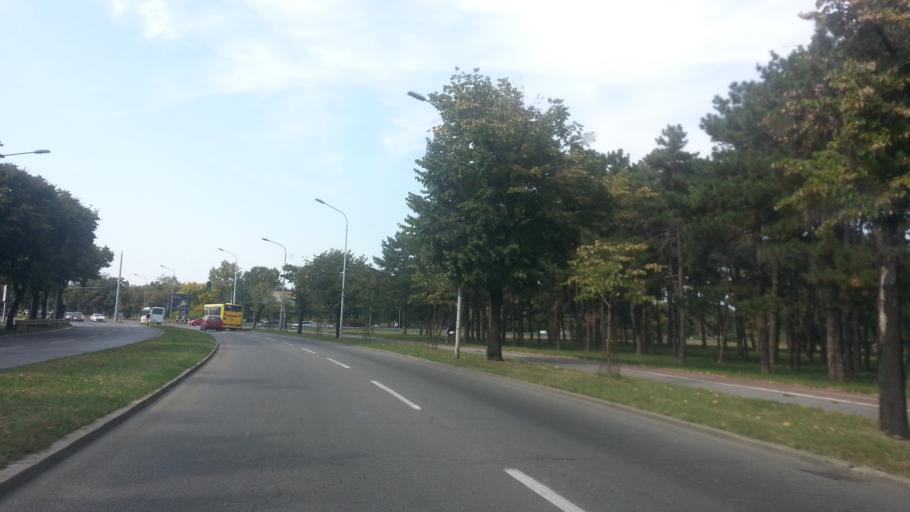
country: RS
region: Central Serbia
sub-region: Belgrade
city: Novi Beograd
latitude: 44.8168
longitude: 20.4385
